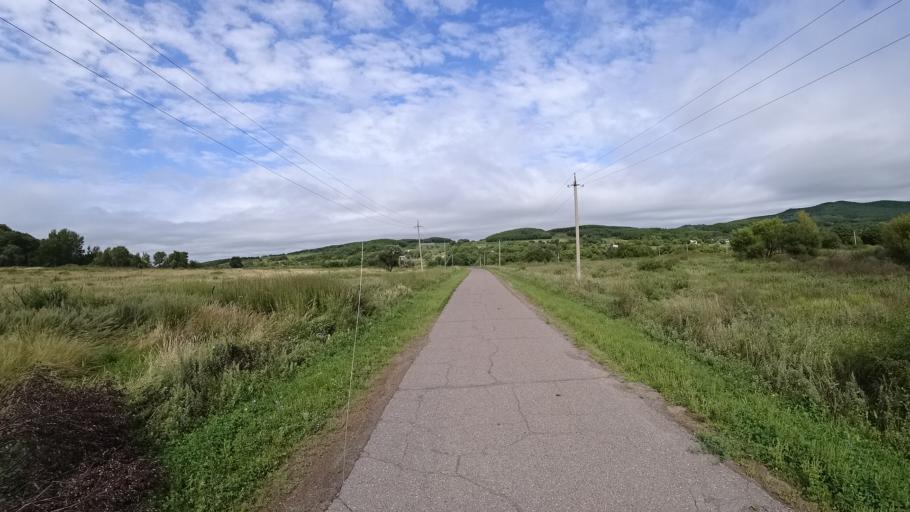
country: RU
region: Primorskiy
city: Lyalichi
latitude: 44.1326
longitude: 132.3877
